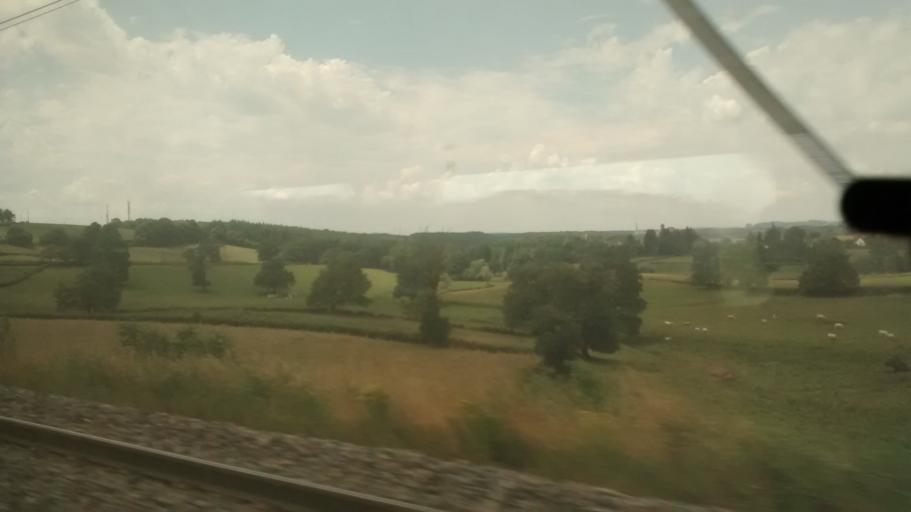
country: FR
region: Bourgogne
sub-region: Departement de Saone-et-Loire
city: Le Breuil
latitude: 46.8013
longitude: 4.4957
